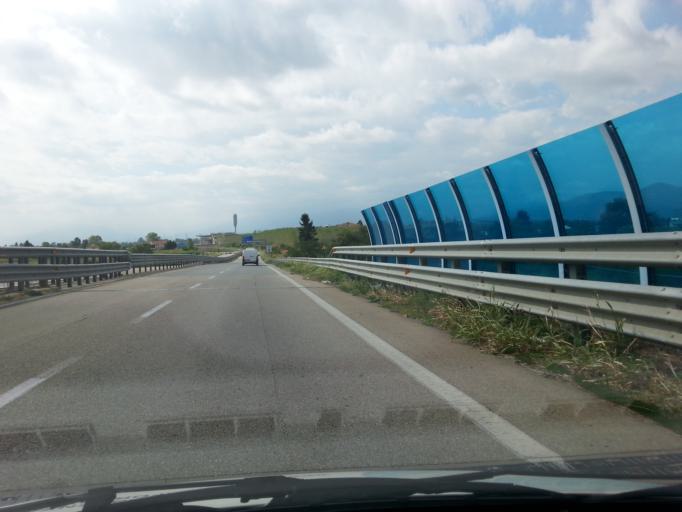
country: IT
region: Piedmont
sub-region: Provincia di Torino
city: Riva
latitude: 44.8949
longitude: 7.3603
